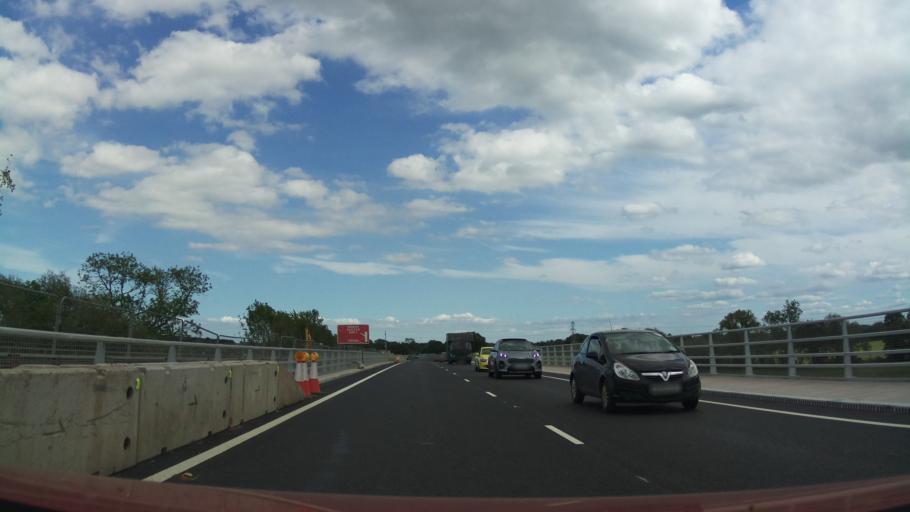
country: GB
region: England
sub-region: Worcestershire
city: Worcester
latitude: 52.1640
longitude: -2.2317
